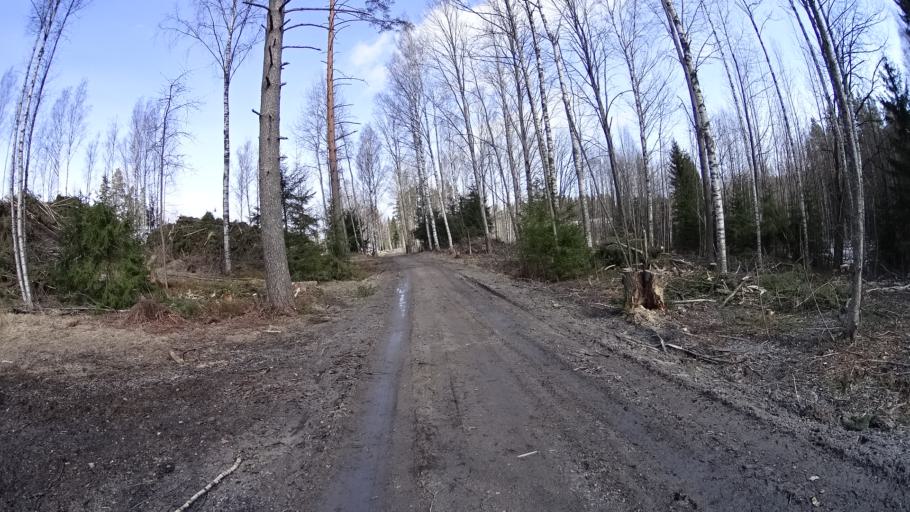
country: FI
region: Uusimaa
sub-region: Helsinki
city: Kilo
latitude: 60.3217
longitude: 24.8169
